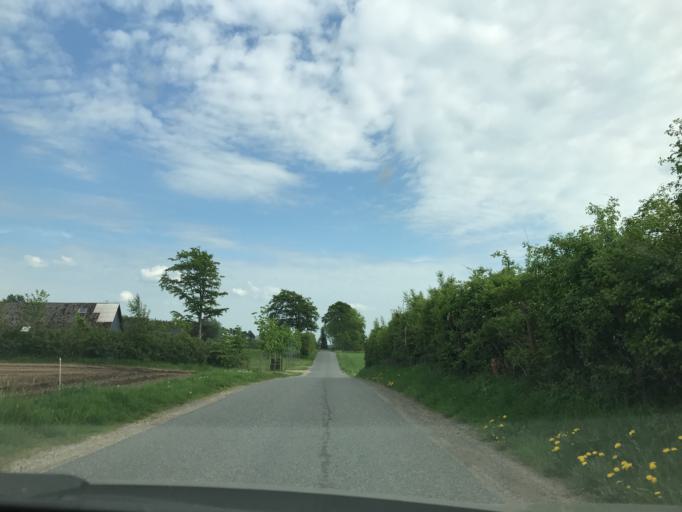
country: DK
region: South Denmark
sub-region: Assens Kommune
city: Assens
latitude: 55.3263
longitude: 9.9068
